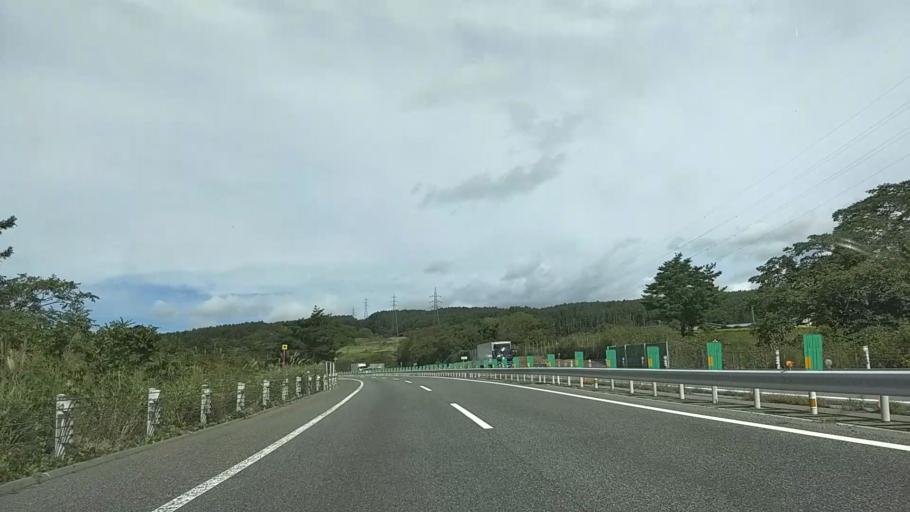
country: JP
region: Nagano
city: Chino
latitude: 35.8848
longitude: 138.2991
